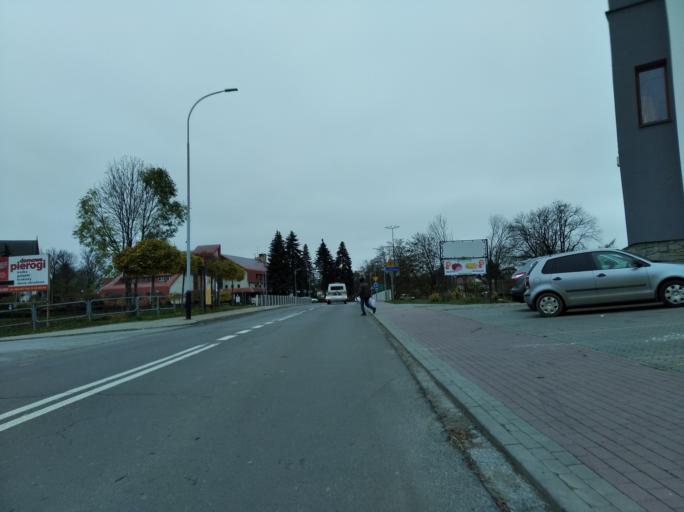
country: PL
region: Subcarpathian Voivodeship
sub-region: Krosno
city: Krosno
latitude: 49.6971
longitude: 21.7620
